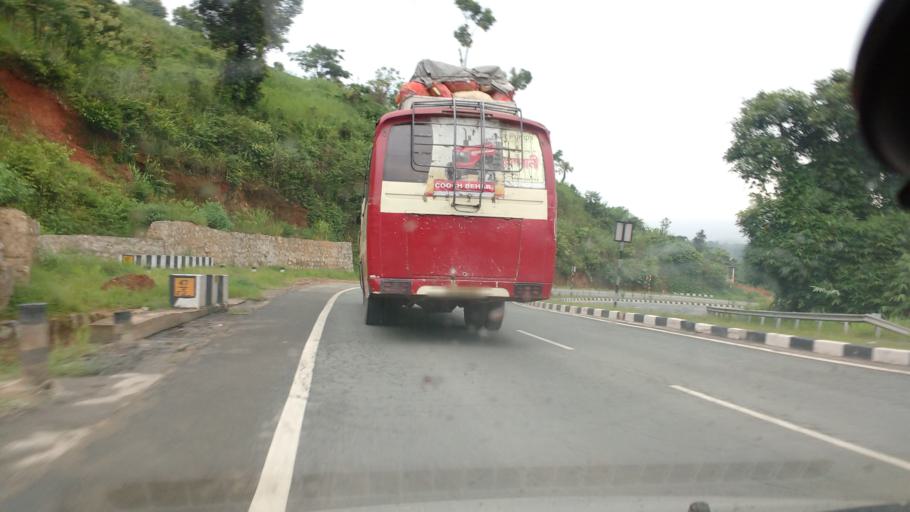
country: IN
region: Meghalaya
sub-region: Ri-Bhoi
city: Nongpoh
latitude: 25.7614
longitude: 91.8784
